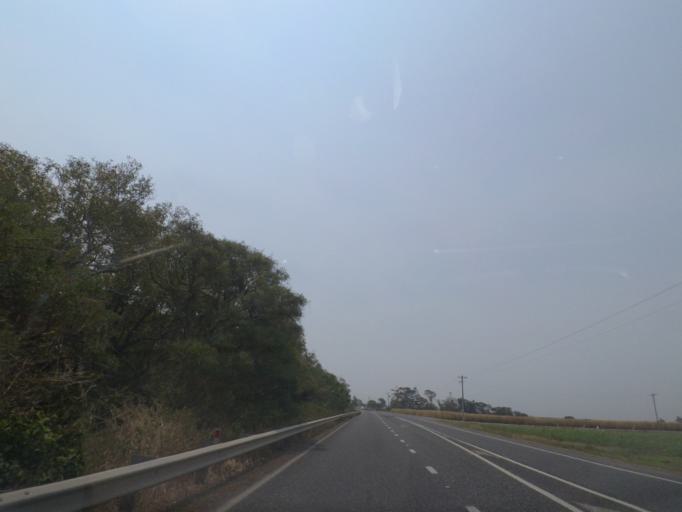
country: AU
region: New South Wales
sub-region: Ballina
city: Ballina
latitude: -28.9688
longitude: 153.4616
